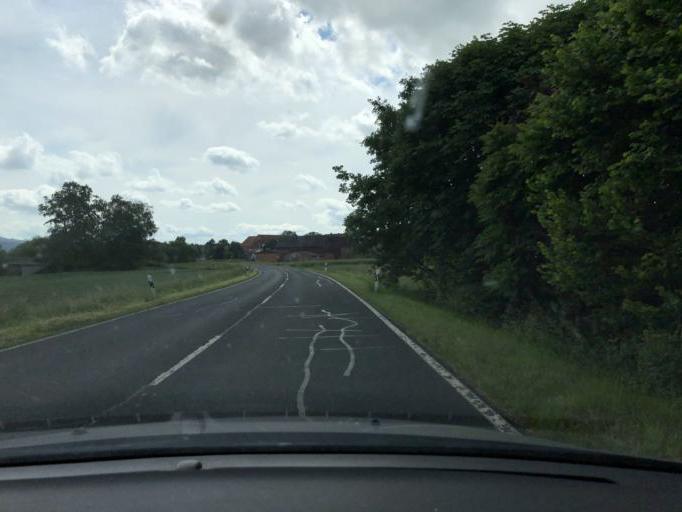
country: DE
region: Hesse
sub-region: Regierungsbezirk Kassel
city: Alheim
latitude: 51.0487
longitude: 9.6238
